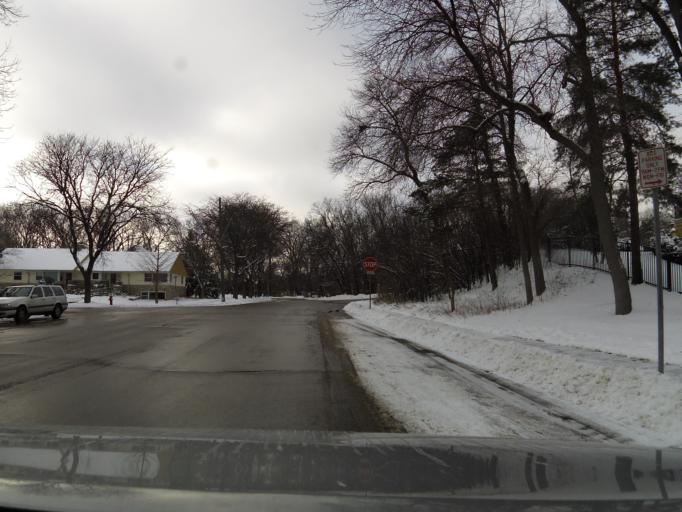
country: US
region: Minnesota
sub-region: Hennepin County
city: Saint Louis Park
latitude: 44.9378
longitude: -93.3209
